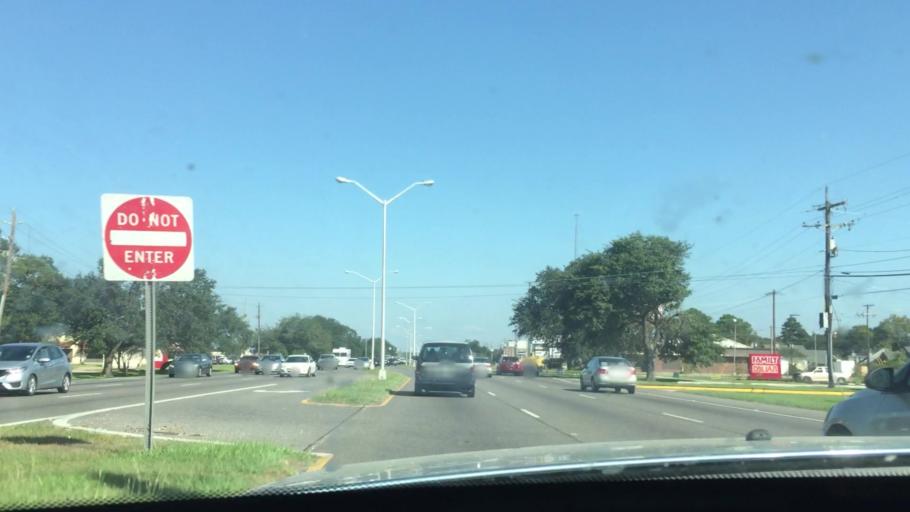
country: US
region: Louisiana
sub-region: East Baton Rouge Parish
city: Baton Rouge
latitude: 30.4515
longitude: -91.1182
